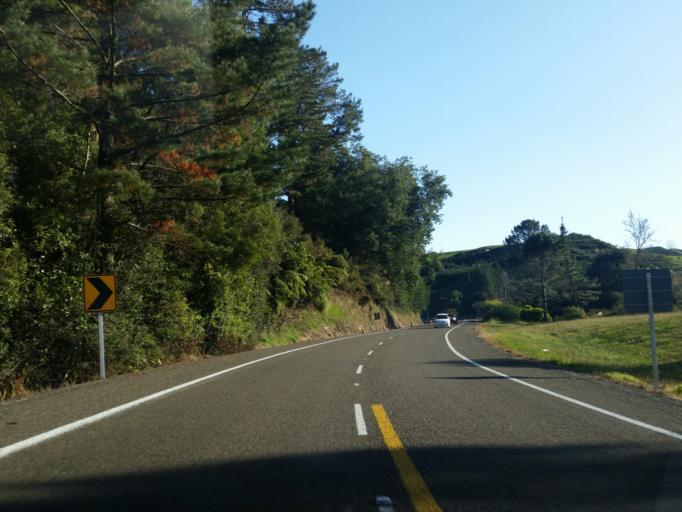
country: NZ
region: Bay of Plenty
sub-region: Western Bay of Plenty District
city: Waihi Beach
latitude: -37.4552
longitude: 175.8935
